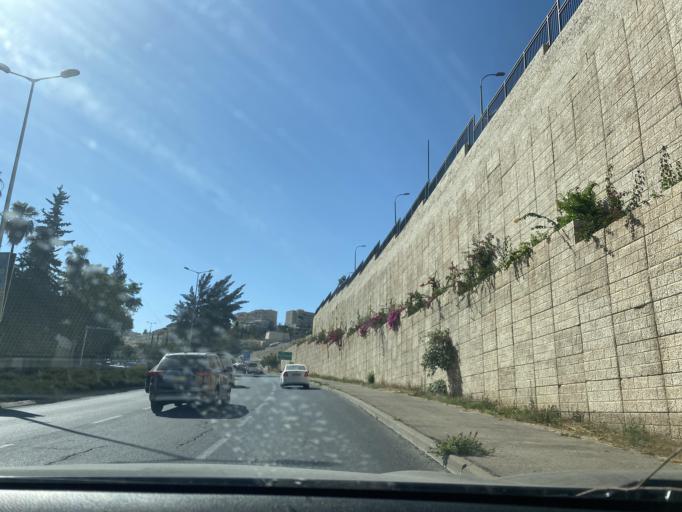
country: PS
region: West Bank
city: Bayt Iksa
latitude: 31.8115
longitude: 35.2031
